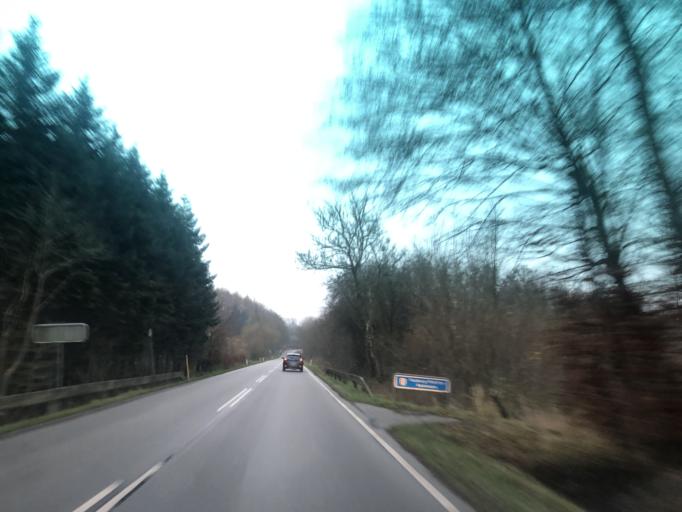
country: DK
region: South Denmark
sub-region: Nyborg Kommune
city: Ullerslev
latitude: 55.2353
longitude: 10.6491
